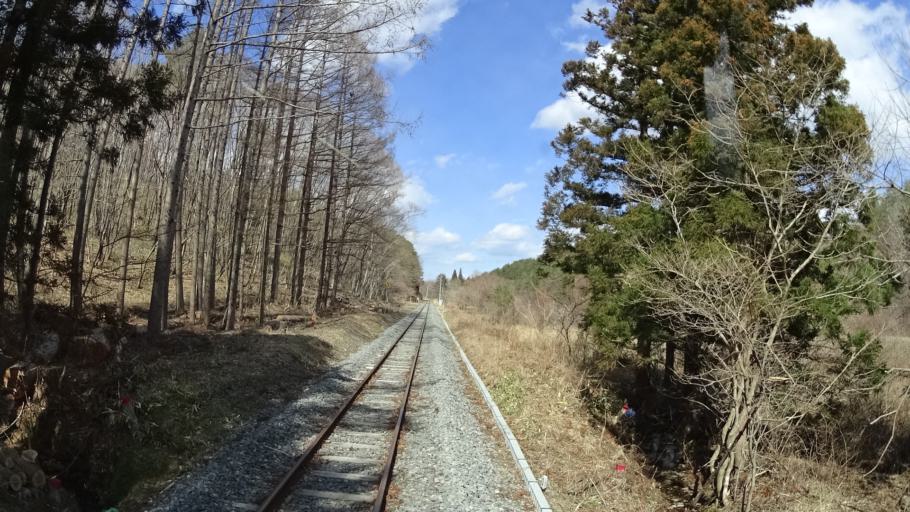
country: JP
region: Iwate
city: Yamada
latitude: 39.4963
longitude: 141.9284
